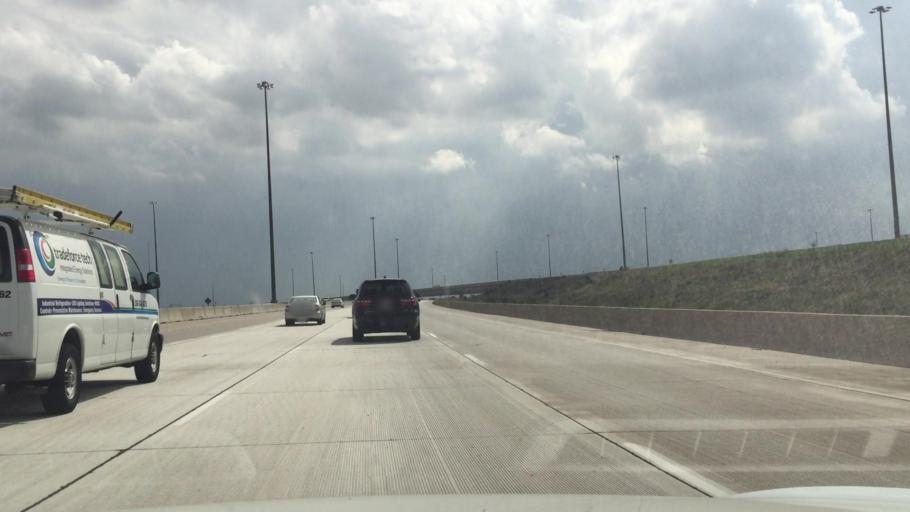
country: CA
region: Ontario
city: Brampton
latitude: 43.6741
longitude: -79.6968
